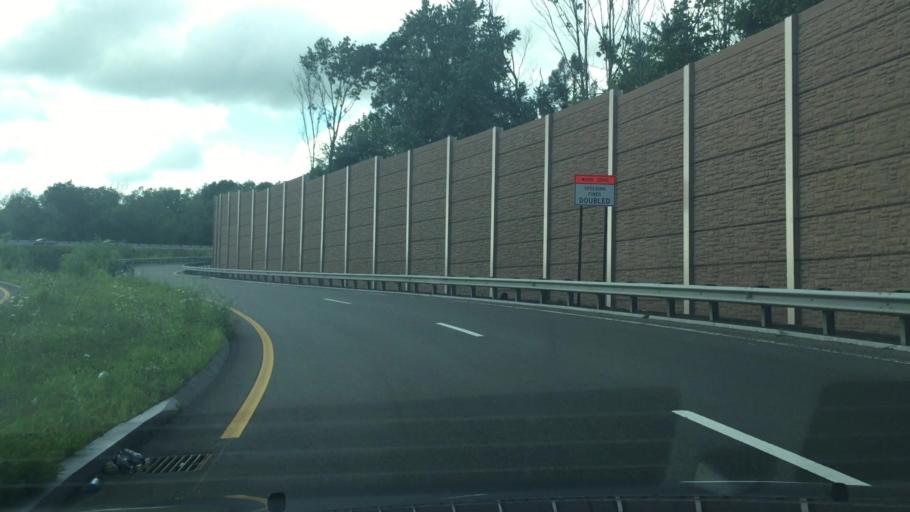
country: US
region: Massachusetts
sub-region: Essex County
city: Methuen
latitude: 42.7068
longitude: -71.2088
